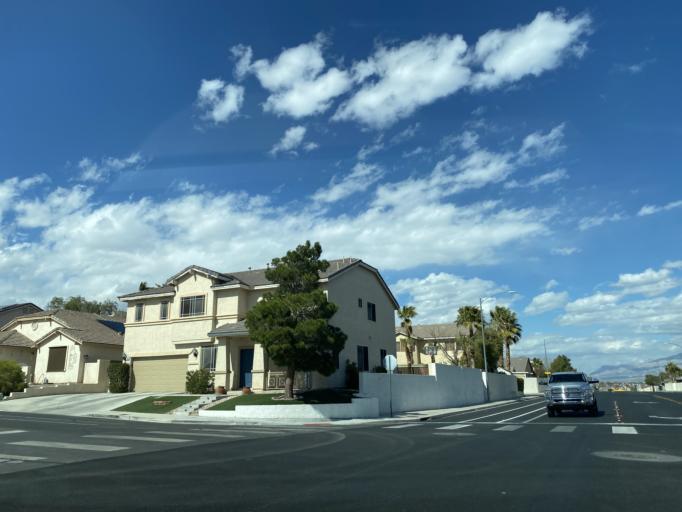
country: US
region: Nevada
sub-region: Clark County
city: Summerlin South
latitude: 36.2295
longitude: -115.3066
